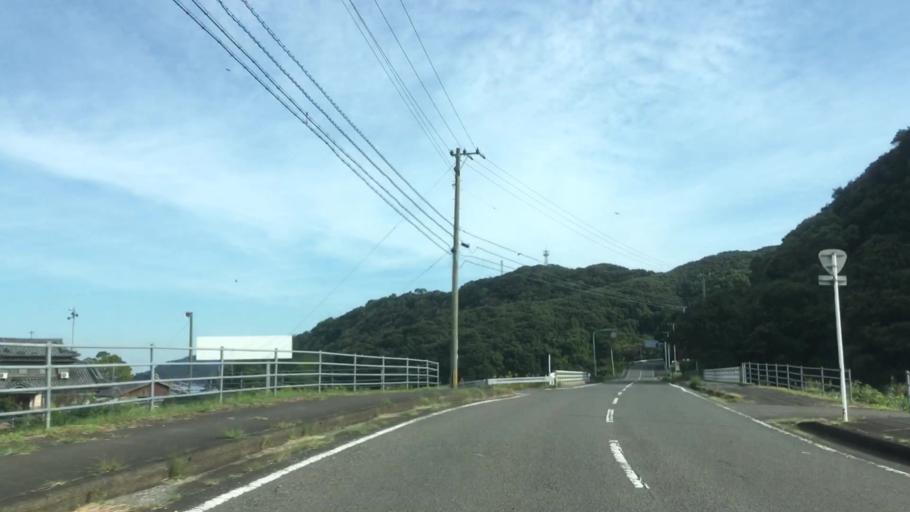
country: JP
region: Nagasaki
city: Sasebo
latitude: 32.9878
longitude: 129.6458
